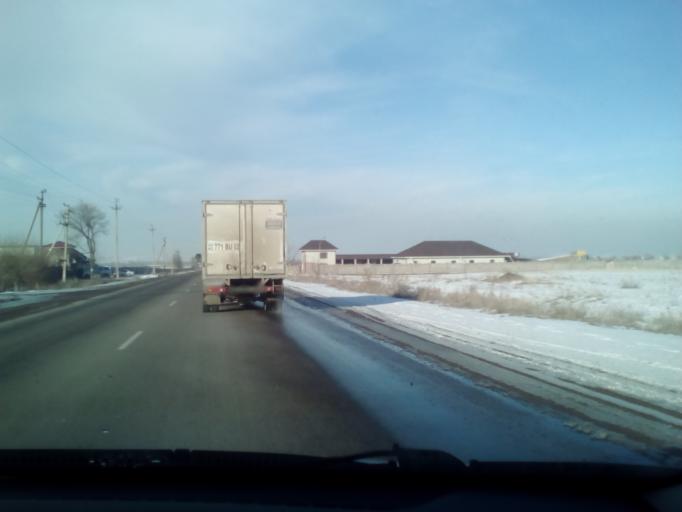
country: KZ
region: Almaty Oblysy
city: Burunday
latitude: 43.2017
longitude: 76.4149
